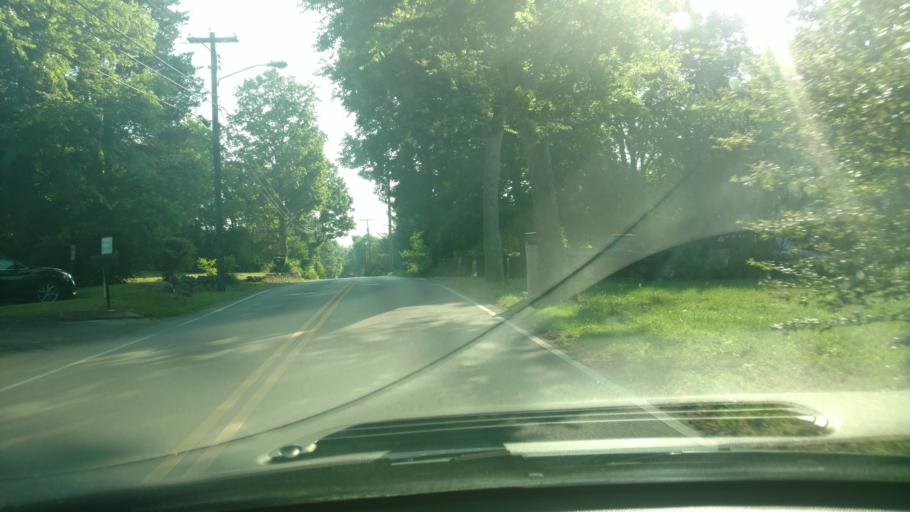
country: US
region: Tennessee
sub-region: Davidson County
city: Lakewood
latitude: 36.2104
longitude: -86.7118
